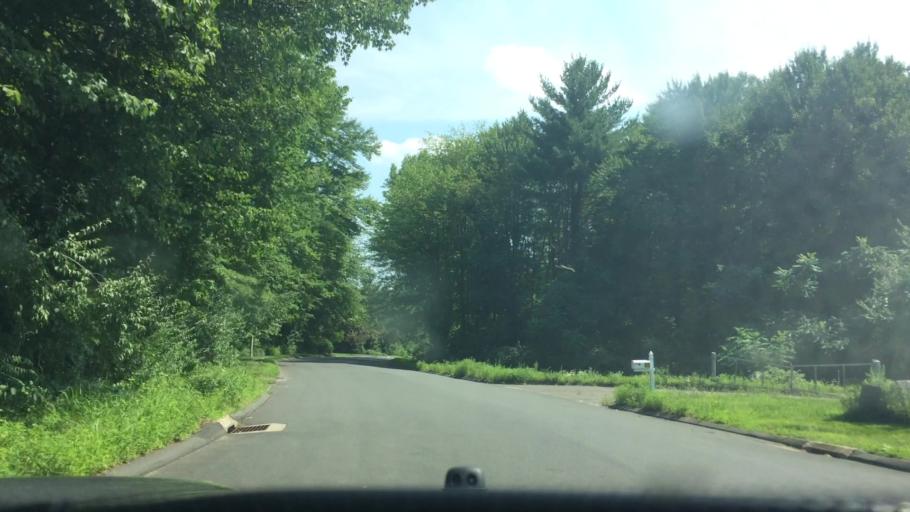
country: US
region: Connecticut
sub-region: Hartford County
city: Tariffville
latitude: 41.8599
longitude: -72.7374
